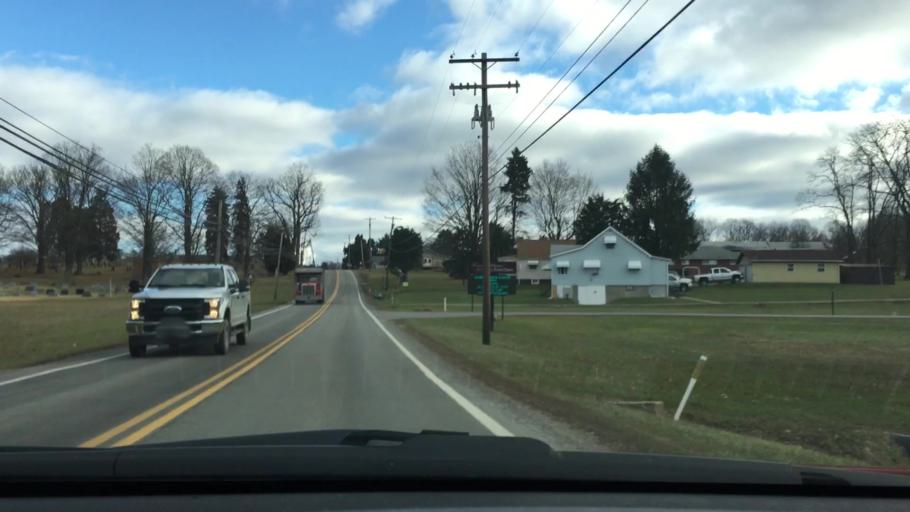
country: US
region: Pennsylvania
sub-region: Armstrong County
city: Orchard Hills
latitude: 40.6057
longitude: -79.4926
